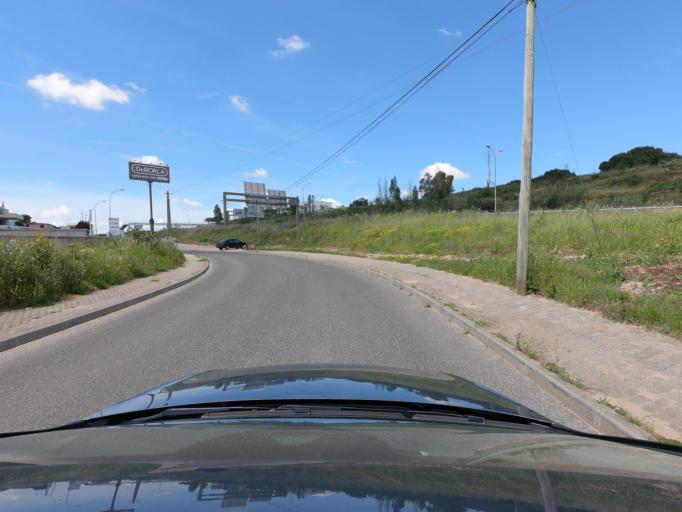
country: PT
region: Lisbon
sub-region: Amadora
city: Amadora
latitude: 38.7421
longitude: -9.2279
